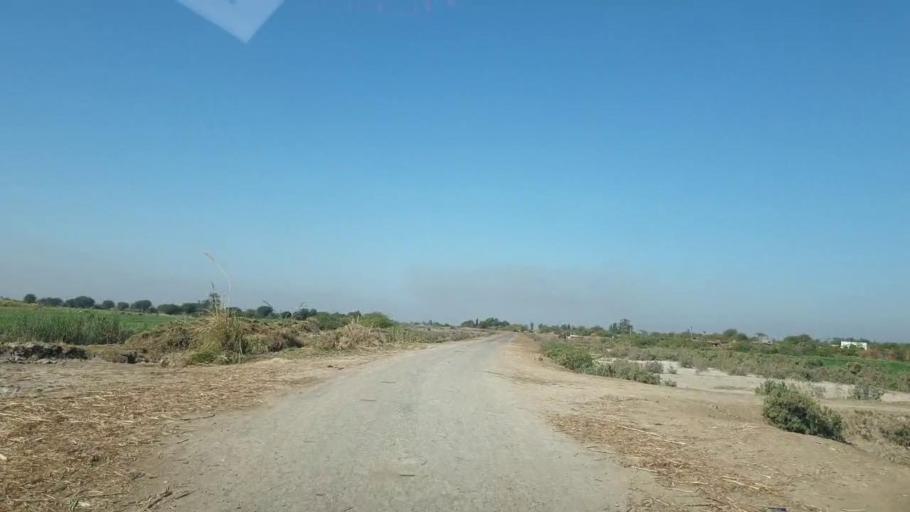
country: PK
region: Sindh
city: Mirpur Khas
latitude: 25.6039
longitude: 69.0425
